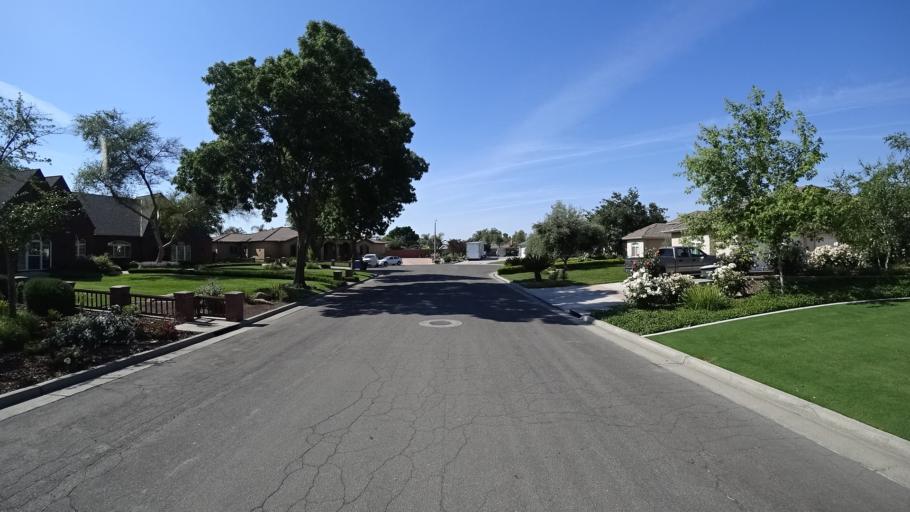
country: US
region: California
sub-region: Kings County
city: Lucerne
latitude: 36.3654
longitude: -119.6417
